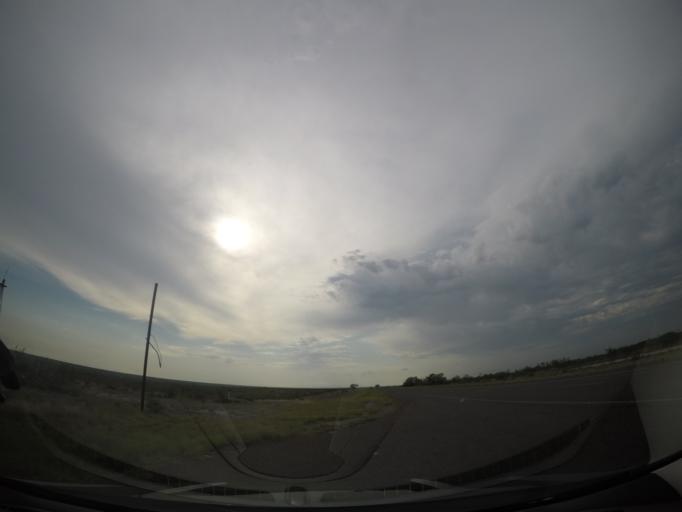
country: US
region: Texas
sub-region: Terrell County
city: Sanderson
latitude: 29.9153
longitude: -101.9107
